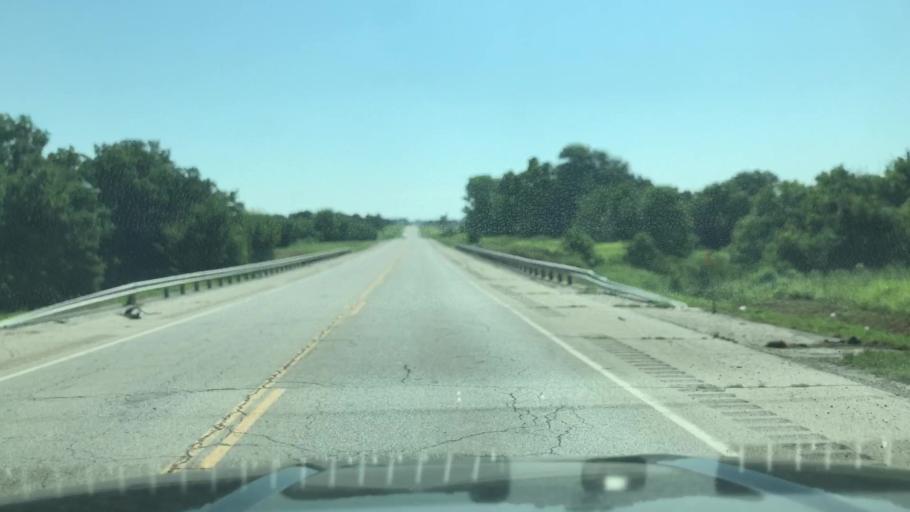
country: US
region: Oklahoma
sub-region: Creek County
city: Drumright
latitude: 35.9885
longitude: -96.5718
